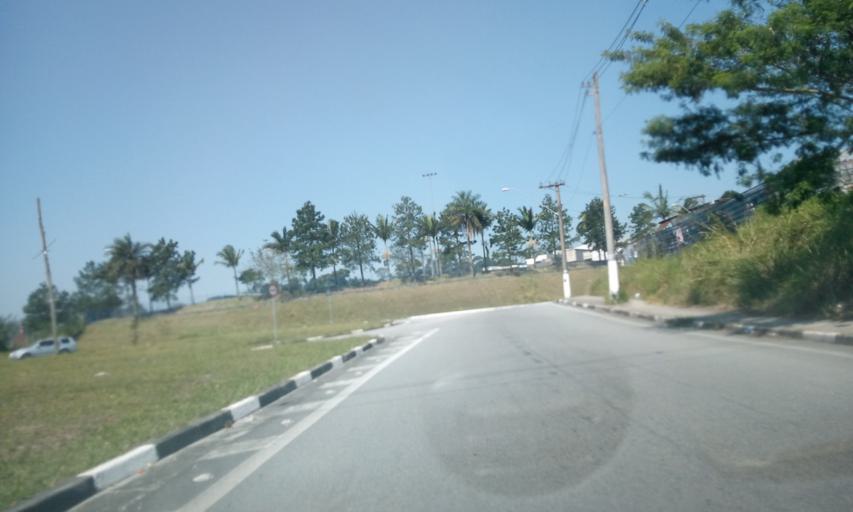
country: BR
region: Sao Paulo
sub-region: Sao Bernardo Do Campo
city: Sao Bernardo do Campo
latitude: -23.7661
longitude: -46.5937
